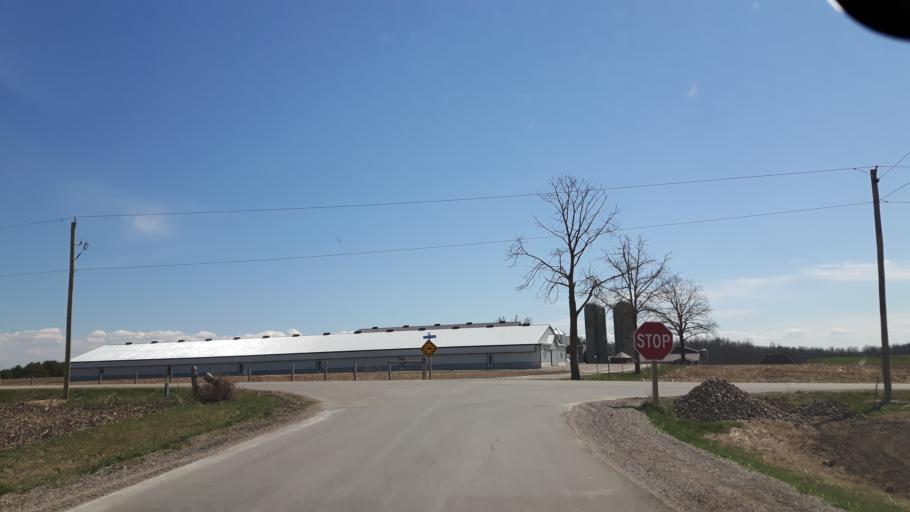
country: CA
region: Ontario
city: Bluewater
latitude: 43.5778
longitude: -81.6438
